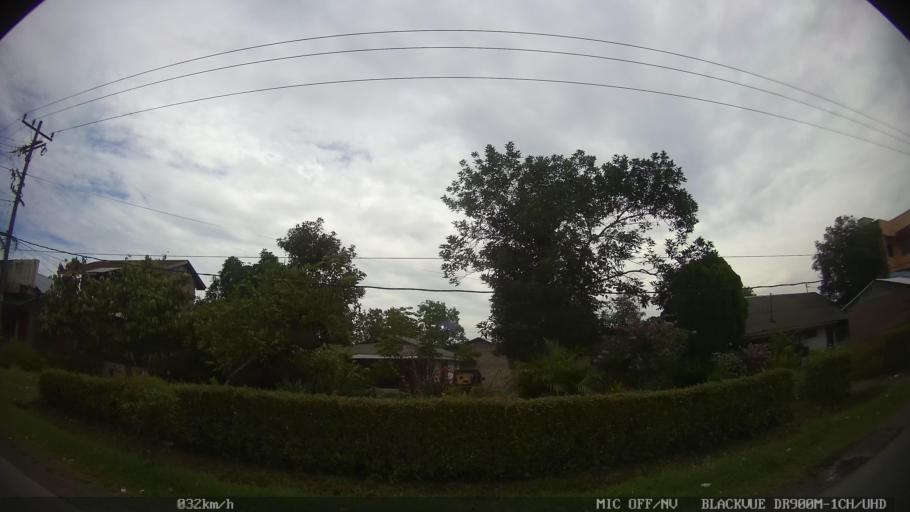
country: ID
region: North Sumatra
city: Sunggal
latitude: 3.6225
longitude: 98.5950
